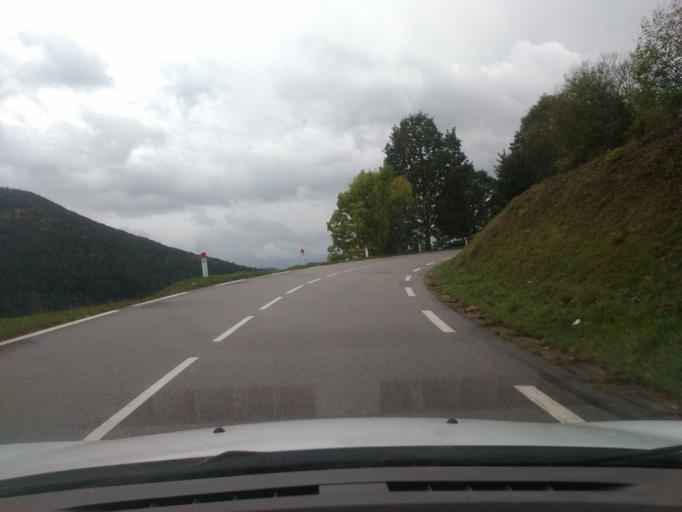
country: FR
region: Lorraine
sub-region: Departement des Vosges
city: Taintrux
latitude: 48.2748
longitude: 6.8909
